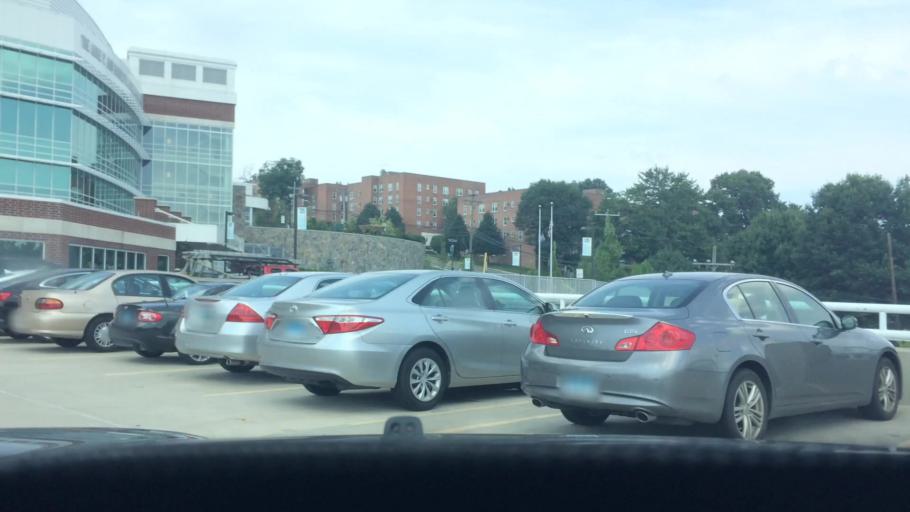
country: US
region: Connecticut
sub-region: Fairfield County
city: Norwalk
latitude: 41.1119
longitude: -73.4209
